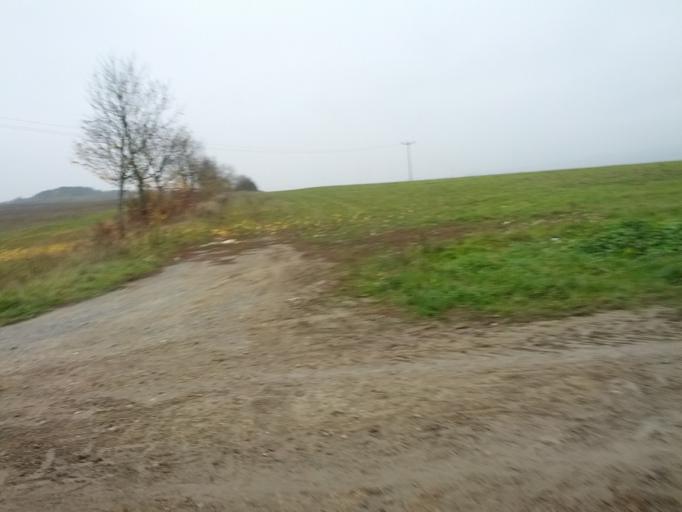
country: DE
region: Thuringia
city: Thal
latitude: 50.9756
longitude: 10.3845
